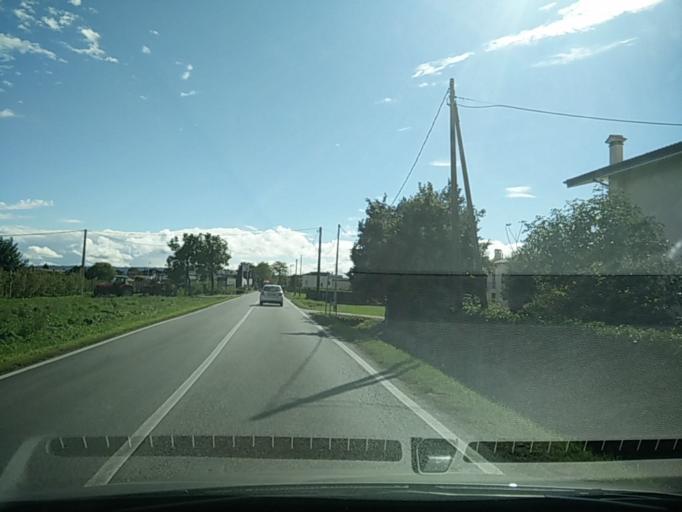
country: IT
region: Veneto
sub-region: Provincia di Treviso
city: Bigolino
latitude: 45.8734
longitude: 12.0045
